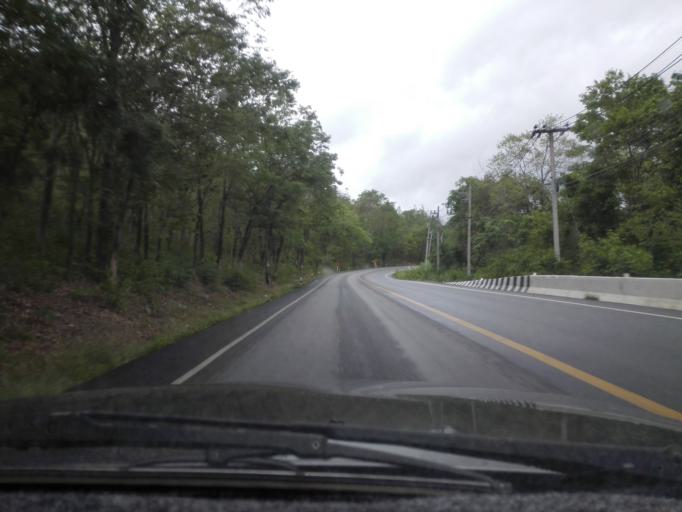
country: TH
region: Tak
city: Tak
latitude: 16.8062
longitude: 98.9961
